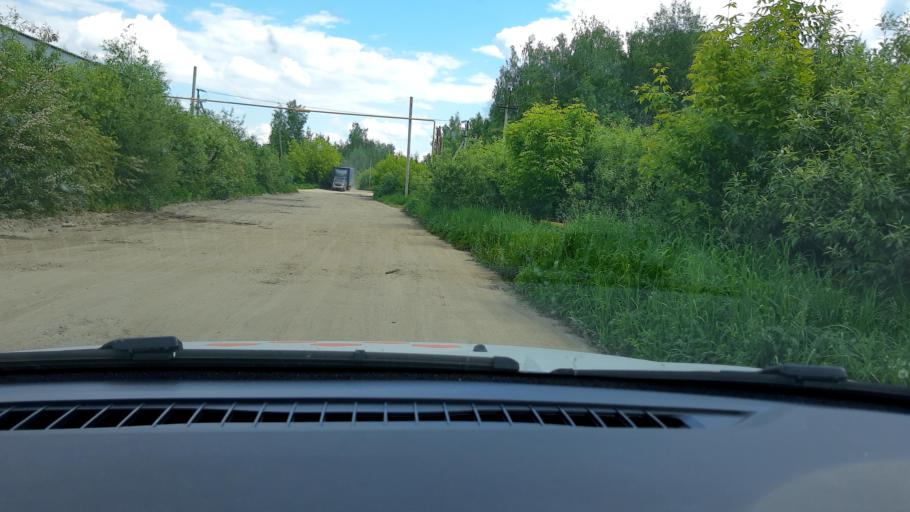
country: RU
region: Nizjnij Novgorod
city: Kstovo
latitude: 56.1711
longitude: 44.1606
